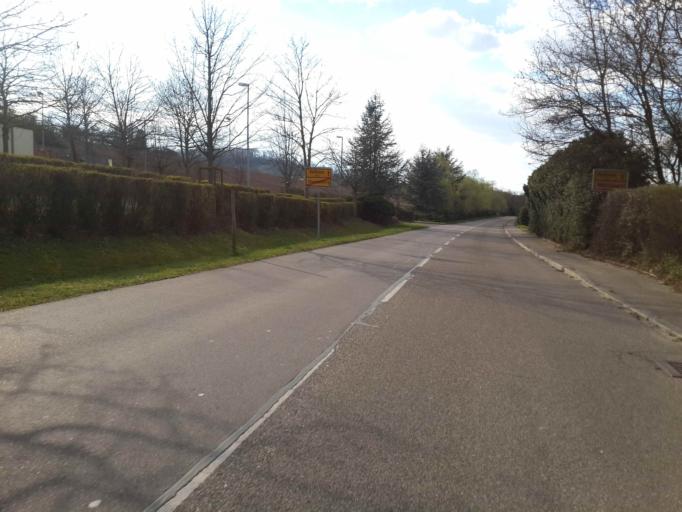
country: DE
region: Baden-Wuerttemberg
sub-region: Regierungsbezirk Stuttgart
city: Weinsberg
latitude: 49.1539
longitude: 9.2728
